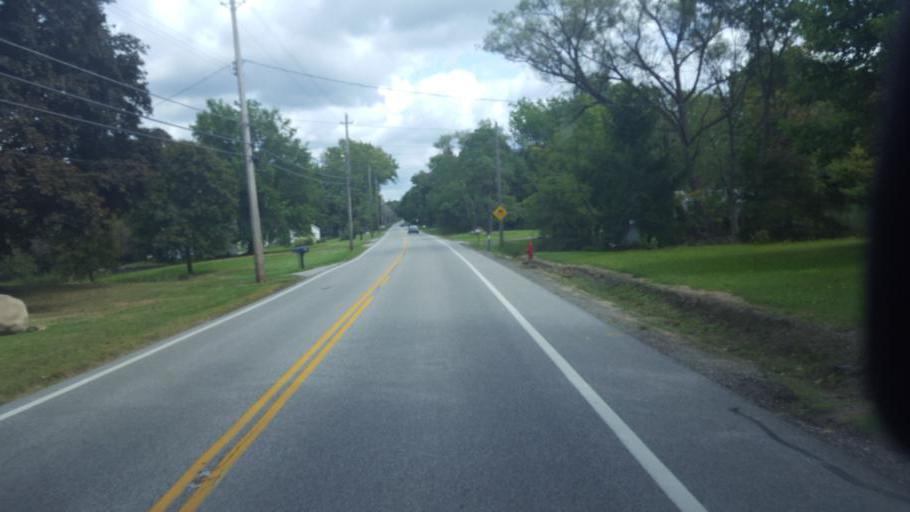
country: US
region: Ohio
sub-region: Lake County
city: Painesville
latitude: 41.7180
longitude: -81.2014
